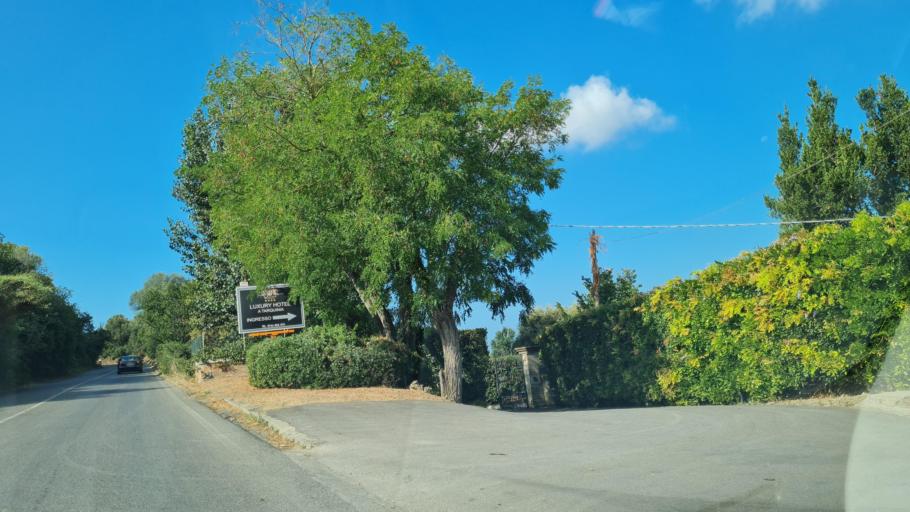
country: IT
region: Latium
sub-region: Provincia di Viterbo
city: Tarquinia
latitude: 42.2551
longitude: 11.7437
